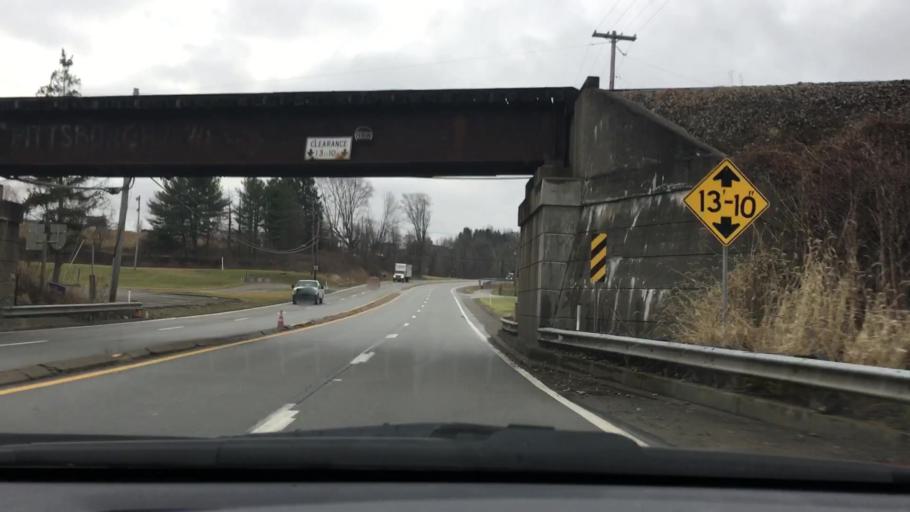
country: US
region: Pennsylvania
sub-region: Westmoreland County
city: West Newton
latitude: 40.1499
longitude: -79.7730
